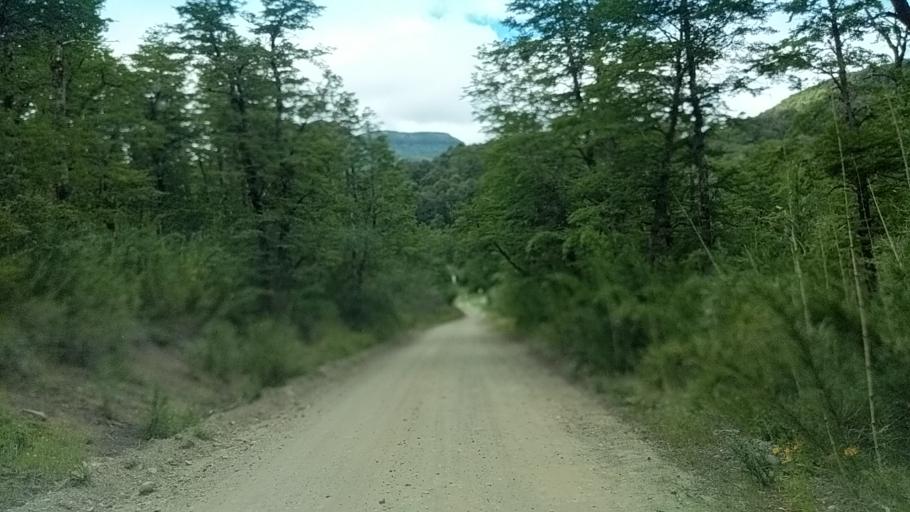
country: AR
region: Neuquen
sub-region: Departamento de Lacar
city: San Martin de los Andes
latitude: -39.8246
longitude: -71.6418
